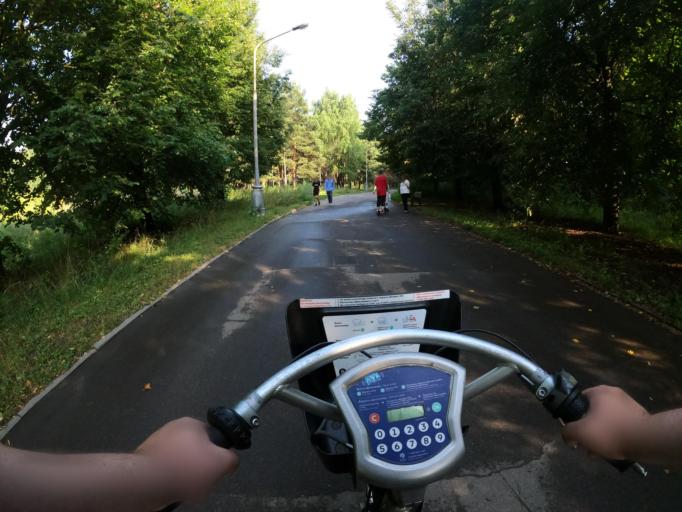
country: RU
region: Moscow
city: Strogino
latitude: 55.8180
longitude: 37.4058
